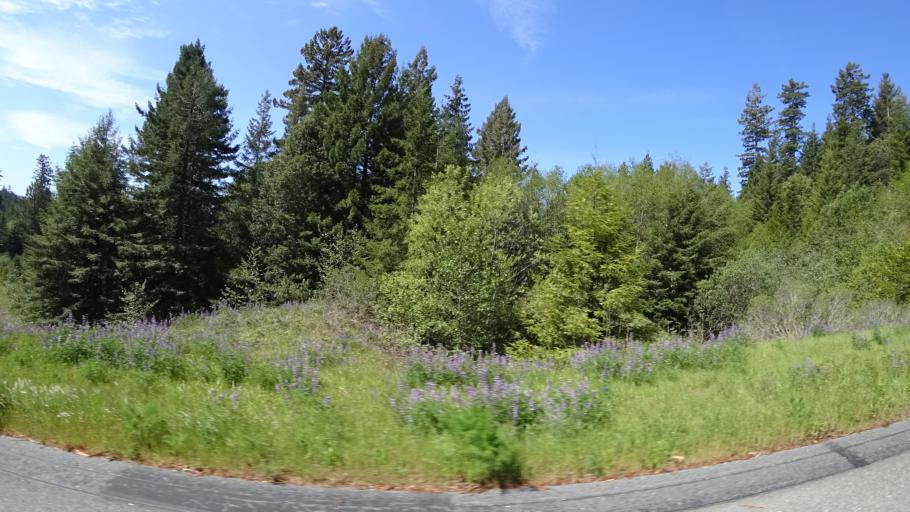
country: US
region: California
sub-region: Humboldt County
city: Westhaven-Moonstone
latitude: 41.3651
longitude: -123.9901
